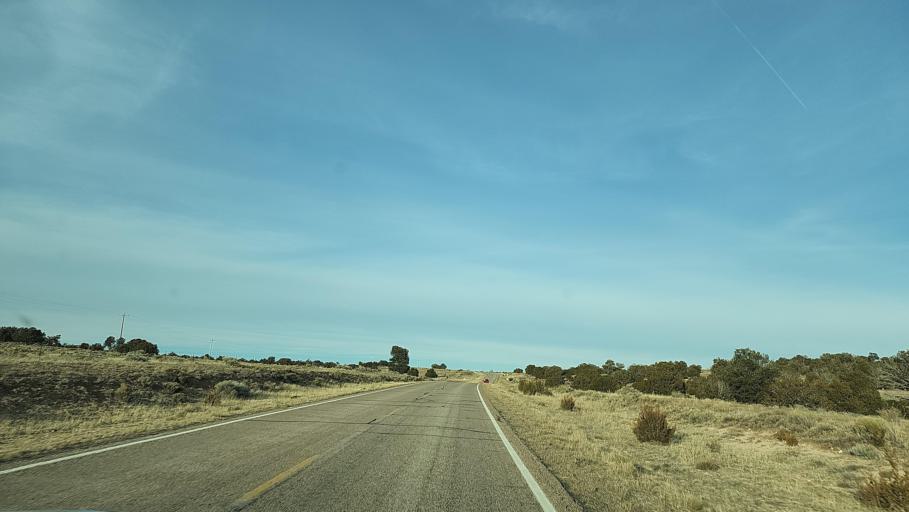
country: US
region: New Mexico
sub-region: Catron County
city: Reserve
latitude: 34.3852
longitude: -108.4539
